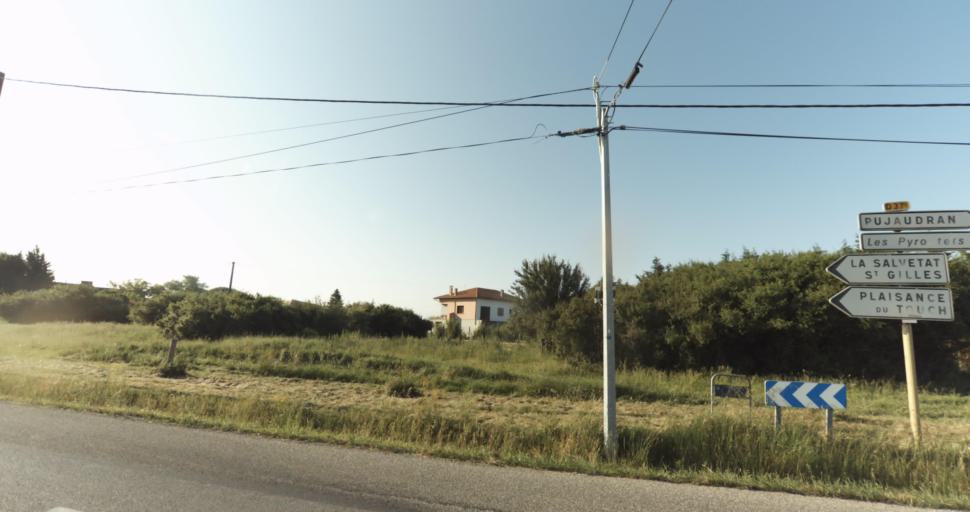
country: FR
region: Midi-Pyrenees
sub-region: Departement de la Haute-Garonne
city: Leguevin
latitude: 43.5758
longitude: 1.2360
